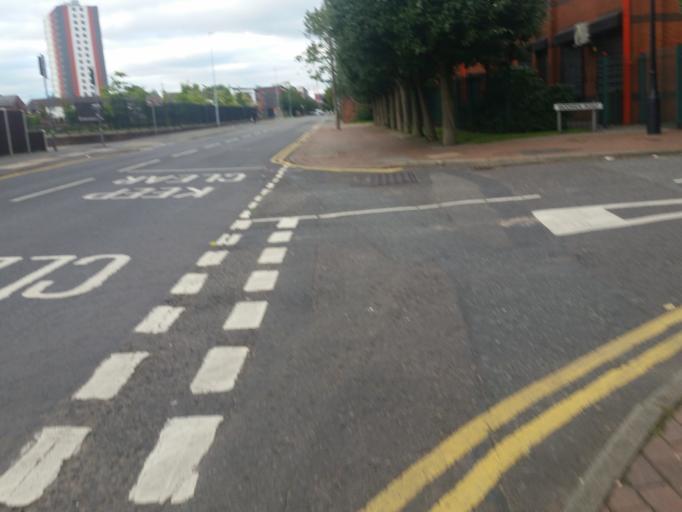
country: GB
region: England
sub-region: City and Borough of Salford
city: Salford
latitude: 53.4682
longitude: -2.2779
